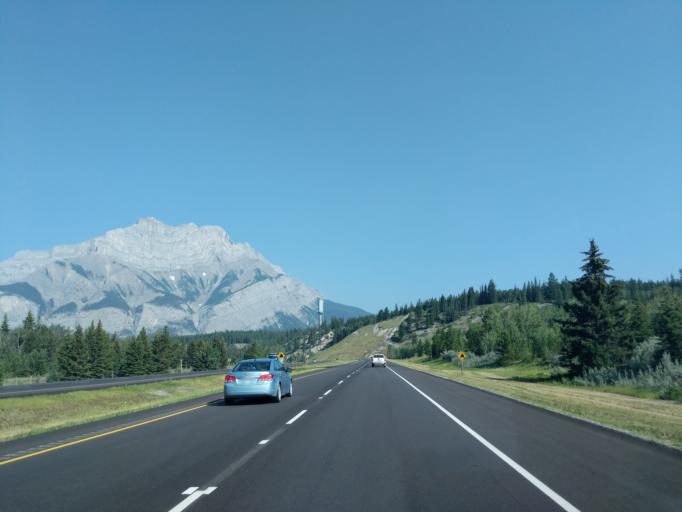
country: CA
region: Alberta
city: Banff
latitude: 51.1943
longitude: -115.4943
